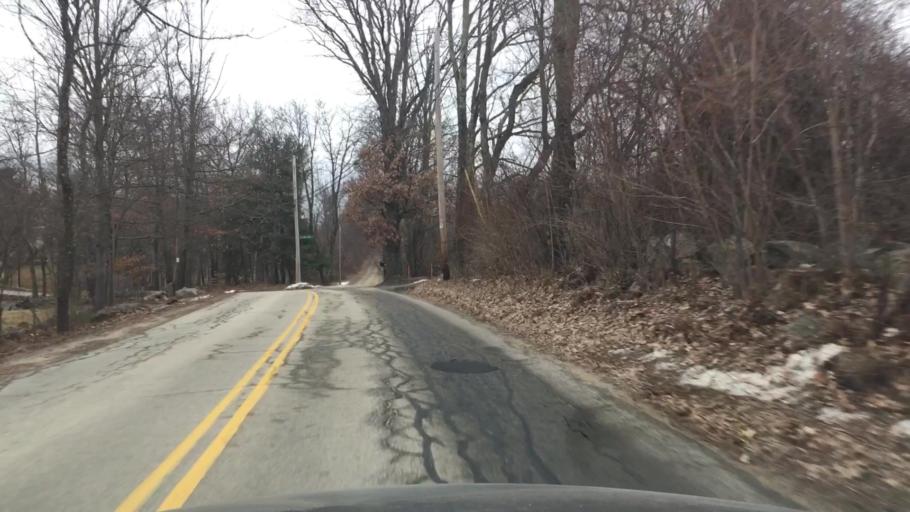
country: US
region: New Hampshire
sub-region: Hillsborough County
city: Mont Vernon
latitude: 42.9340
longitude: -71.6082
